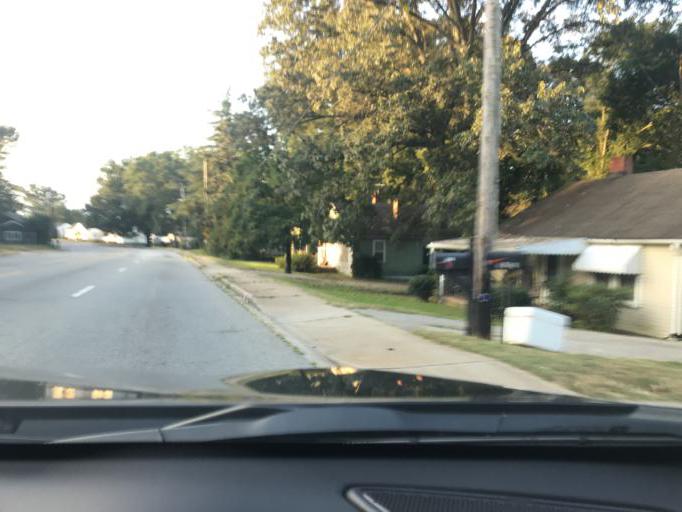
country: US
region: South Carolina
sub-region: Greenville County
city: Welcome
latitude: 34.8309
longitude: -82.4389
